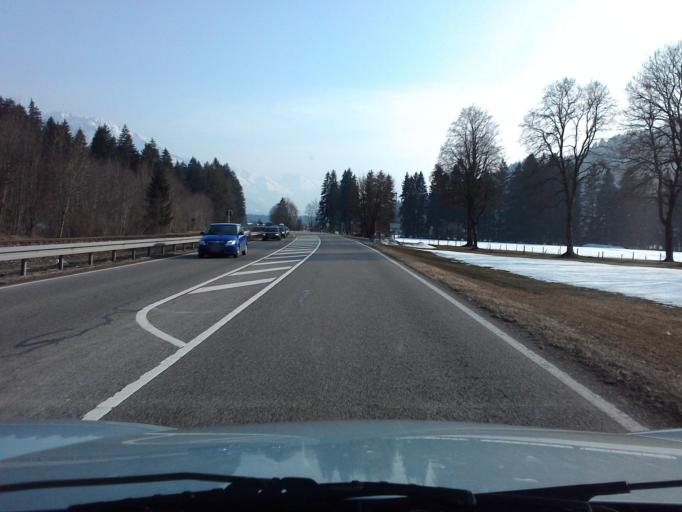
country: DE
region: Bavaria
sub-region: Swabia
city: Obermaiselstein
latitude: 47.4480
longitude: 10.2727
